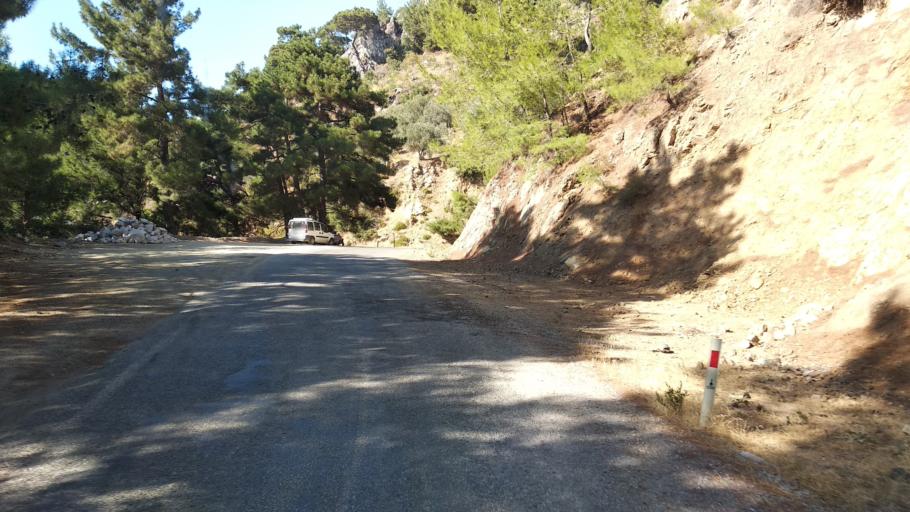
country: TR
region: Izmir
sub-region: Seferihisar
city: Seferhisar
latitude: 38.3183
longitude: 26.9581
